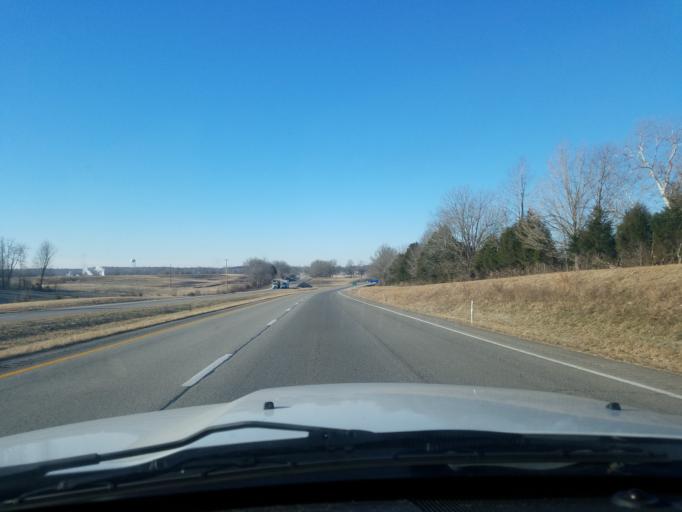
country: US
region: Kentucky
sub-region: Ohio County
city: Beaver Dam
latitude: 37.3818
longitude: -86.8148
